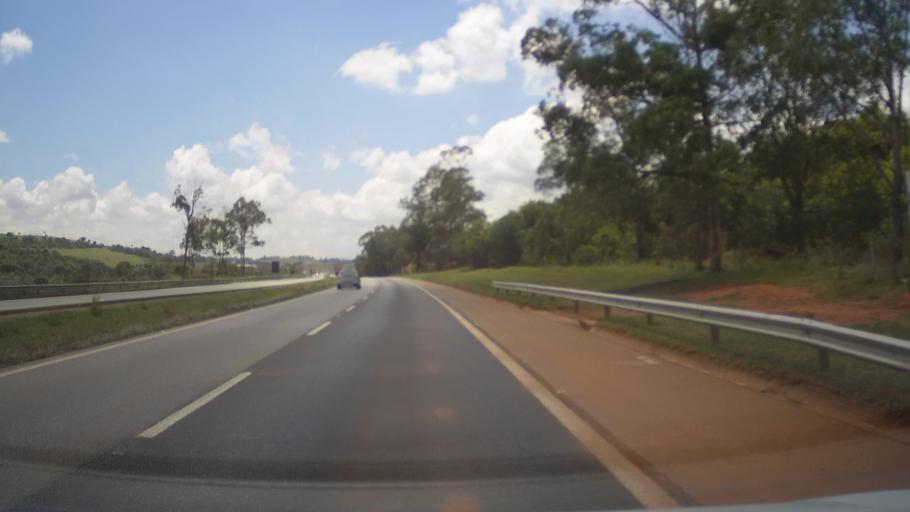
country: BR
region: Minas Gerais
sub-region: Sao Goncalo Do Sapucai
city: Sao Goncalo do Sapucai
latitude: -21.9192
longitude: -45.5976
